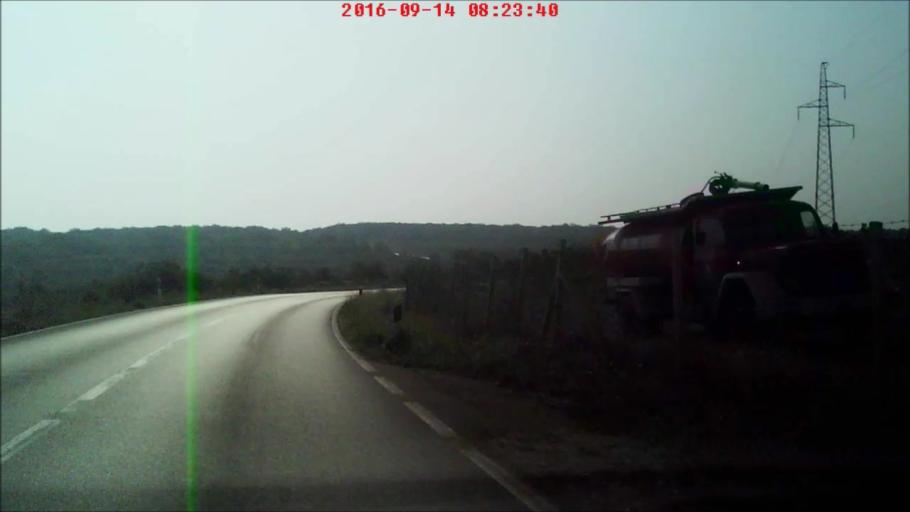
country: HR
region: Zadarska
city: Vrsi
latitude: 44.2109
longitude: 15.2340
